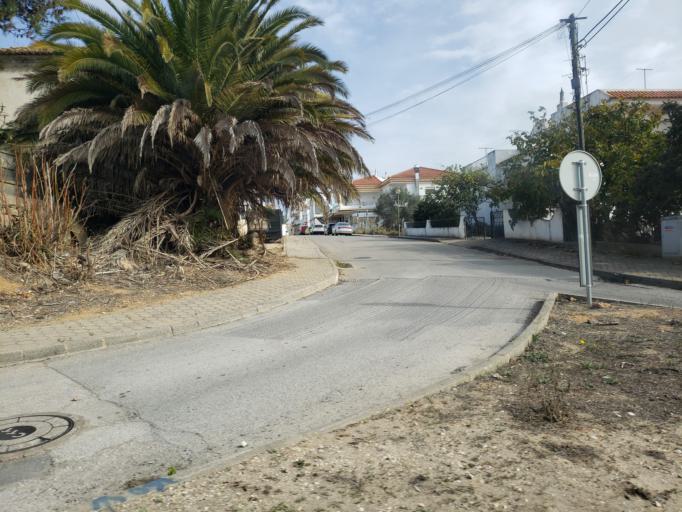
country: PT
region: Faro
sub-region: Portimao
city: Portimao
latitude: 37.1537
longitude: -8.5599
